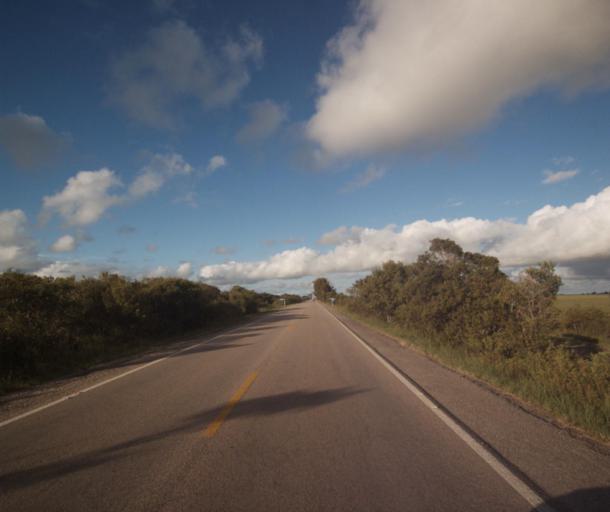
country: BR
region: Rio Grande do Sul
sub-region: Rio Grande
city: Rio Grande
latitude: -32.1819
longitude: -52.4243
